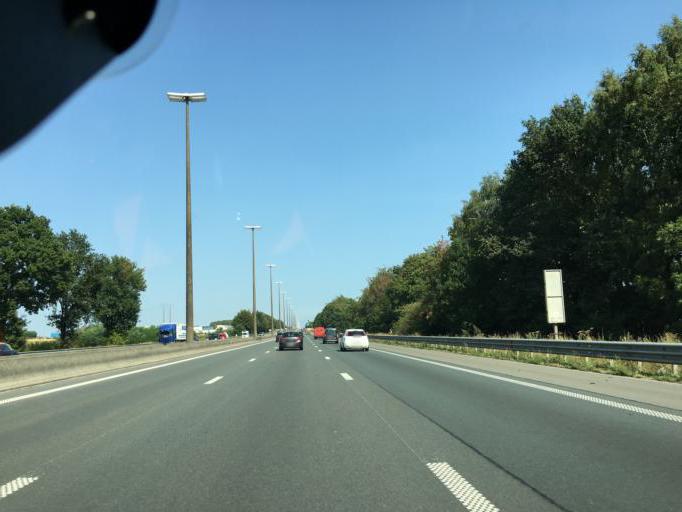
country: BE
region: Wallonia
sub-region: Province du Hainaut
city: Fleurus
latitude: 50.4819
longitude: 4.5847
